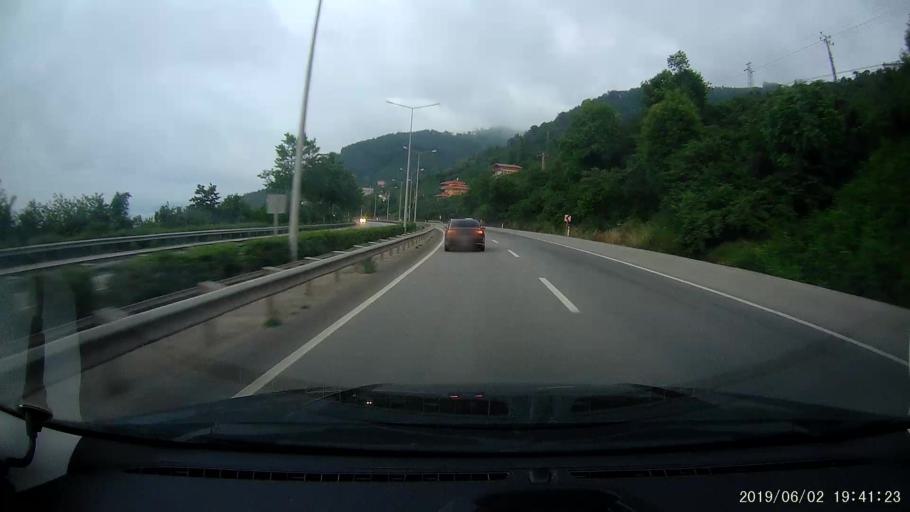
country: TR
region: Giresun
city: Kesap
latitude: 40.9139
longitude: 38.4791
